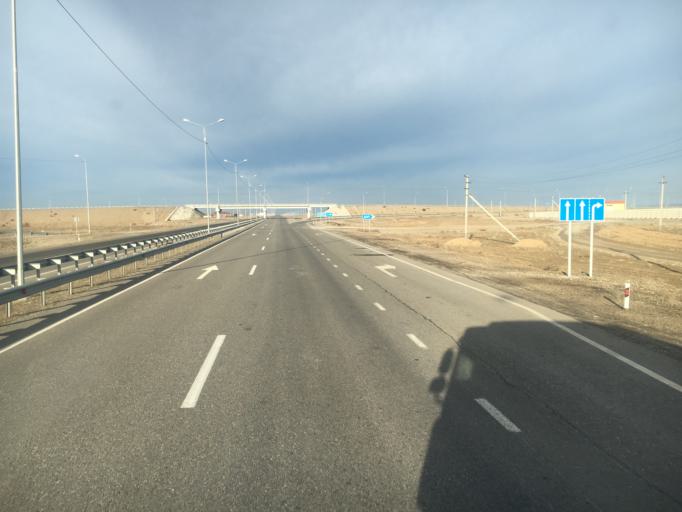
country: KZ
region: Ongtustik Qazaqstan
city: Turkestan
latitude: 43.4132
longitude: 68.0287
